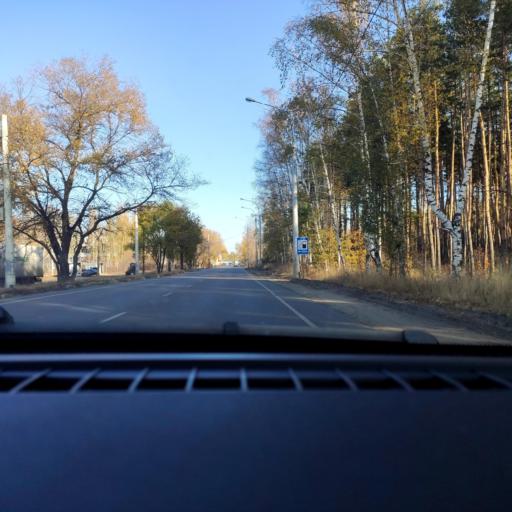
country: RU
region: Voronezj
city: Somovo
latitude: 51.7158
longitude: 39.2937
